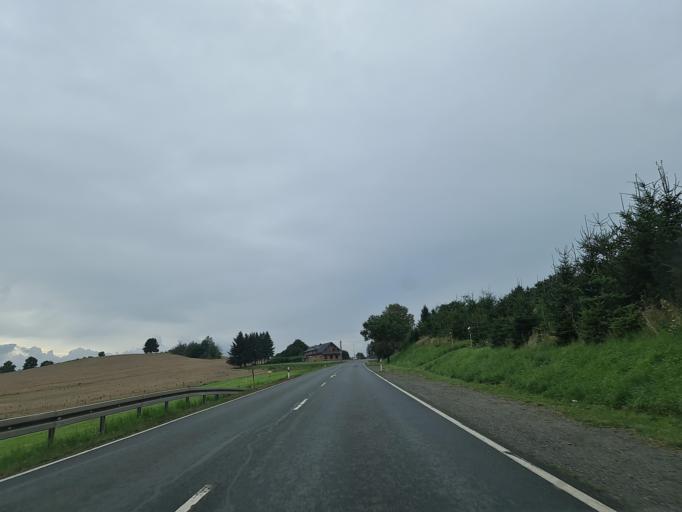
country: DE
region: Saxony
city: Oelsnitz
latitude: 50.4317
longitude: 12.1708
